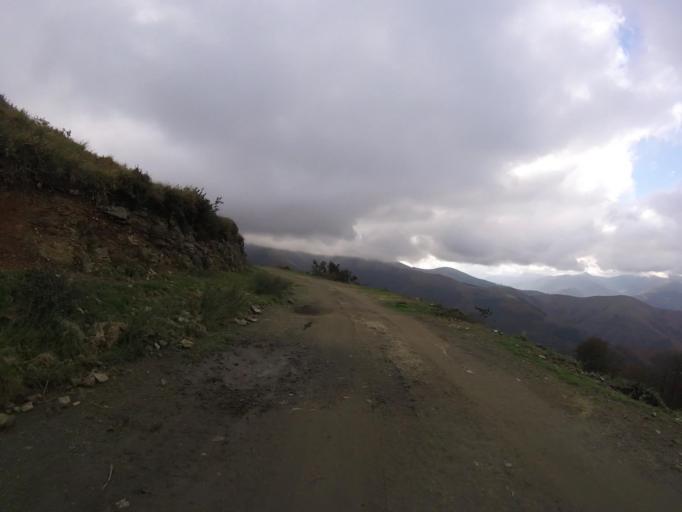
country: ES
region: Navarre
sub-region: Provincia de Navarra
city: Goizueta
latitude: 43.1966
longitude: -1.8233
